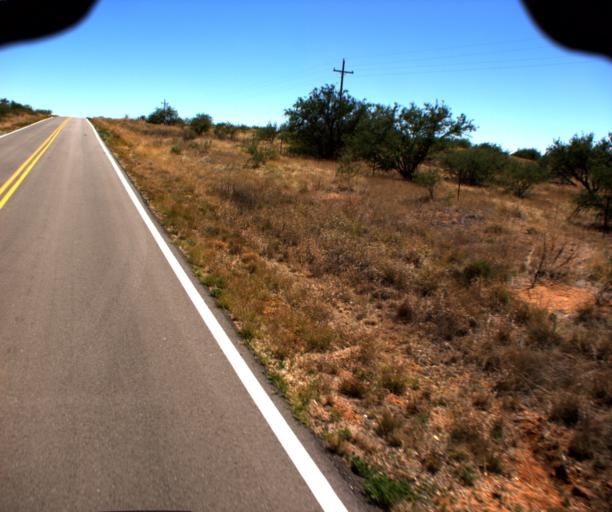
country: US
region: Arizona
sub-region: Pima County
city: Sells
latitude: 31.5561
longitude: -111.5392
